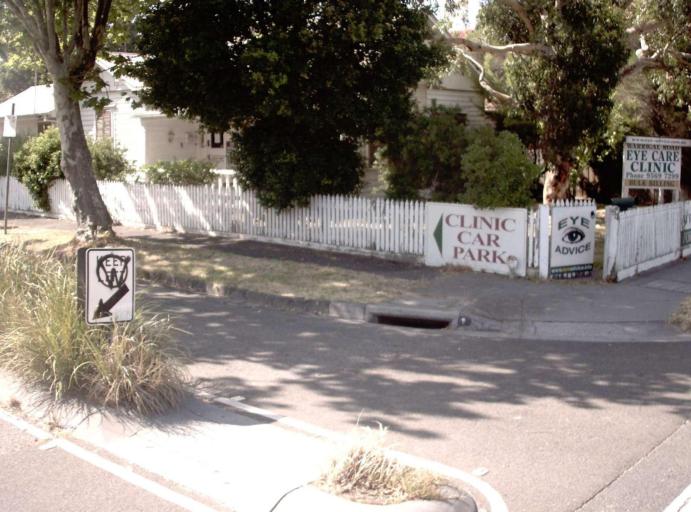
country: AU
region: Victoria
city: Hughesdale
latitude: -37.9026
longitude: 145.0864
